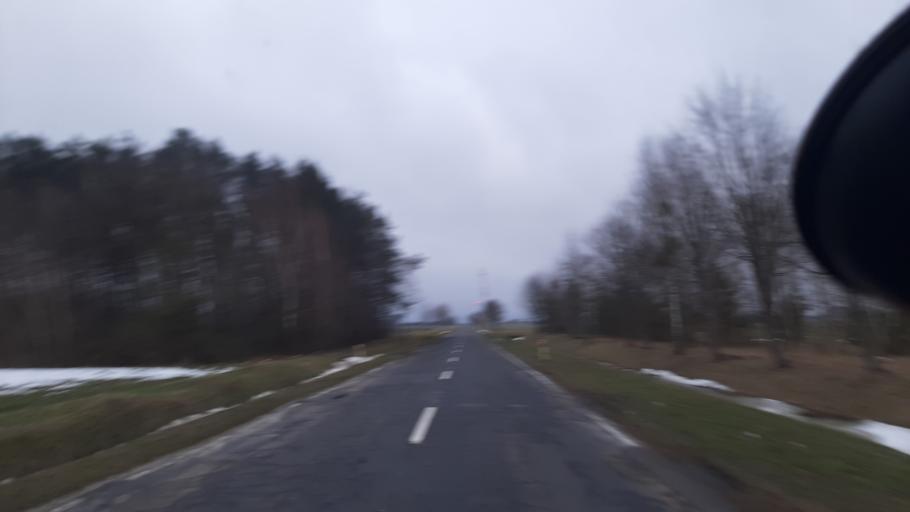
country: PL
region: Lublin Voivodeship
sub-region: Powiat wlodawski
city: Hansk
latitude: 51.5599
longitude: 23.3256
